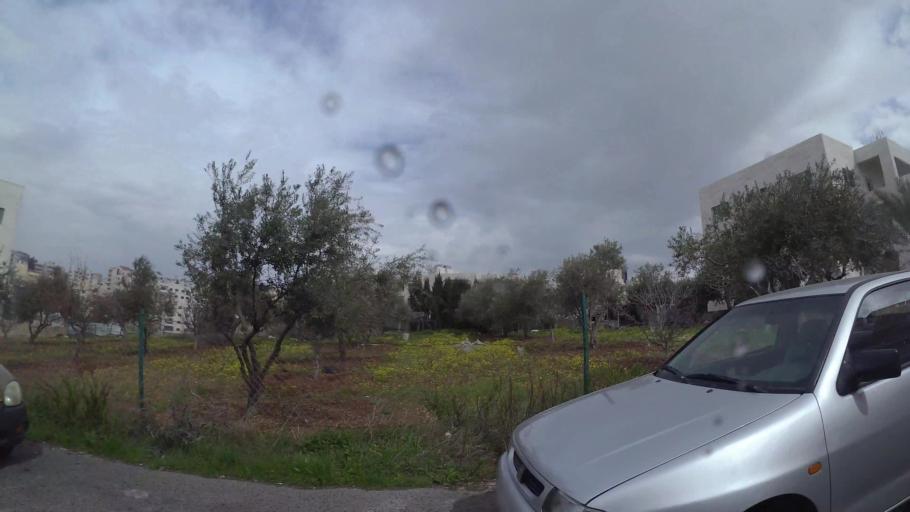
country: JO
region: Amman
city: Umm as Summaq
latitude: 31.9087
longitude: 35.8502
